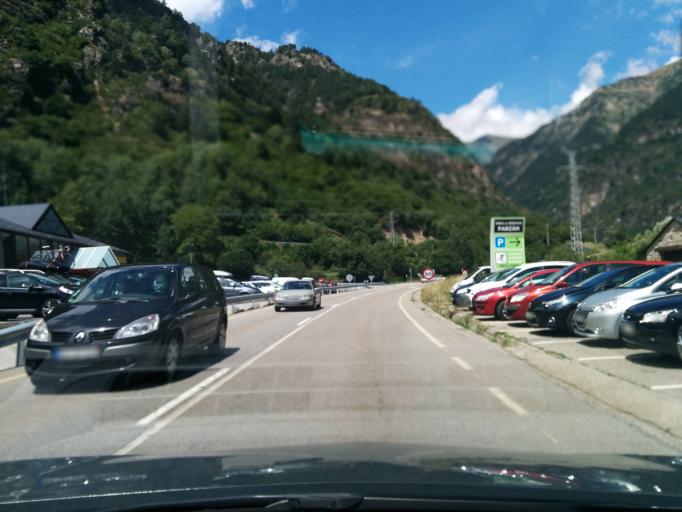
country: ES
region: Aragon
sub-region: Provincia de Huesca
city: Bielsa
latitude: 42.6616
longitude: 0.2093
